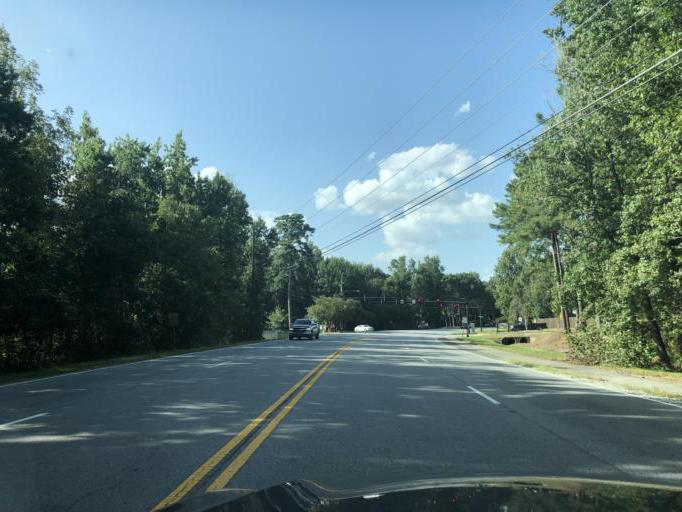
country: US
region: Georgia
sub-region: Muscogee County
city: Columbus
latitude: 32.4929
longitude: -84.8958
